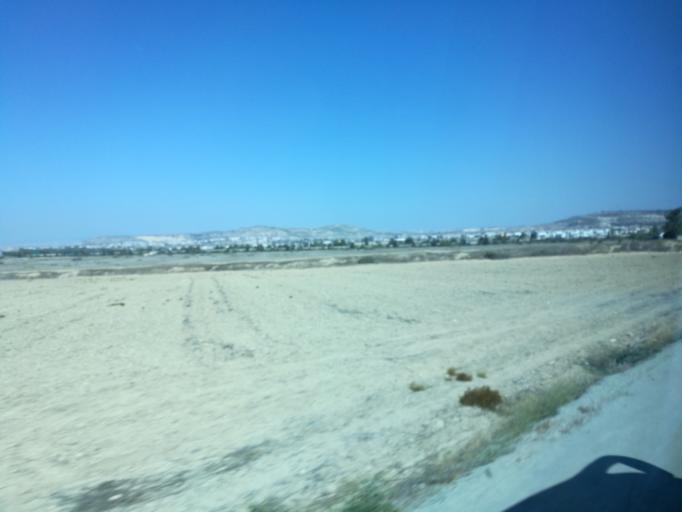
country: CY
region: Larnaka
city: Pyla
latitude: 34.9876
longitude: 33.6983
